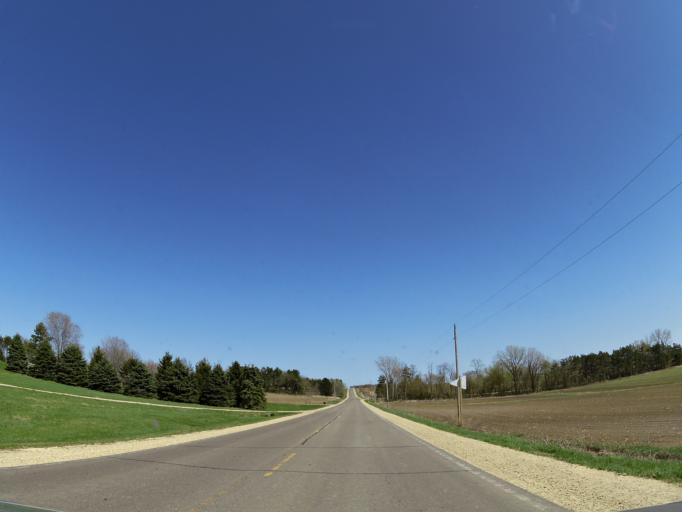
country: US
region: Wisconsin
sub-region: Saint Croix County
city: Hammond
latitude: 44.9346
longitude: -92.4692
